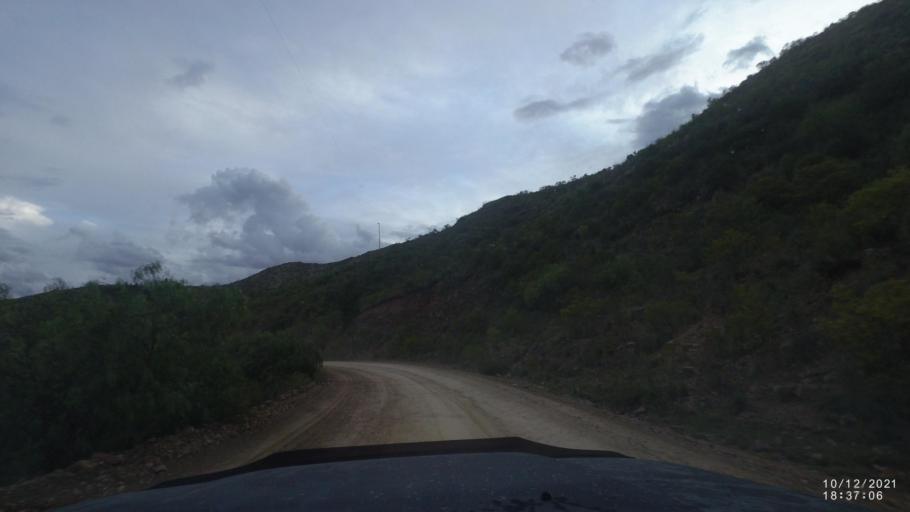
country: BO
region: Cochabamba
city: Tarata
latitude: -17.8361
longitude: -65.9929
